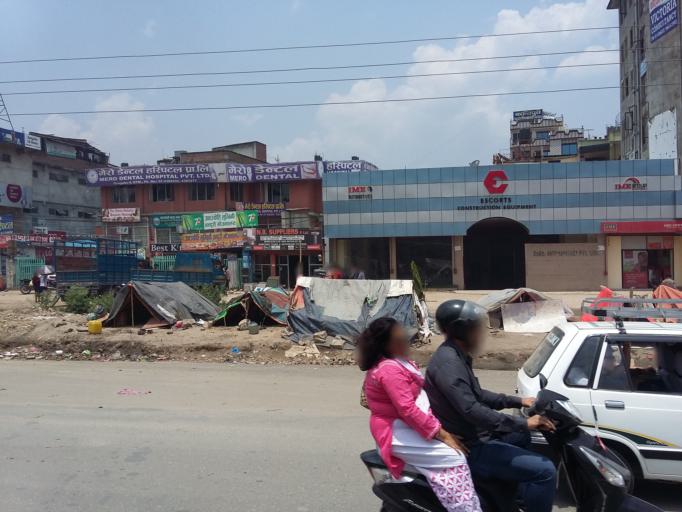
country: NP
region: Central Region
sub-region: Bagmati Zone
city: Kathmandu
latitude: 27.7352
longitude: 85.3151
